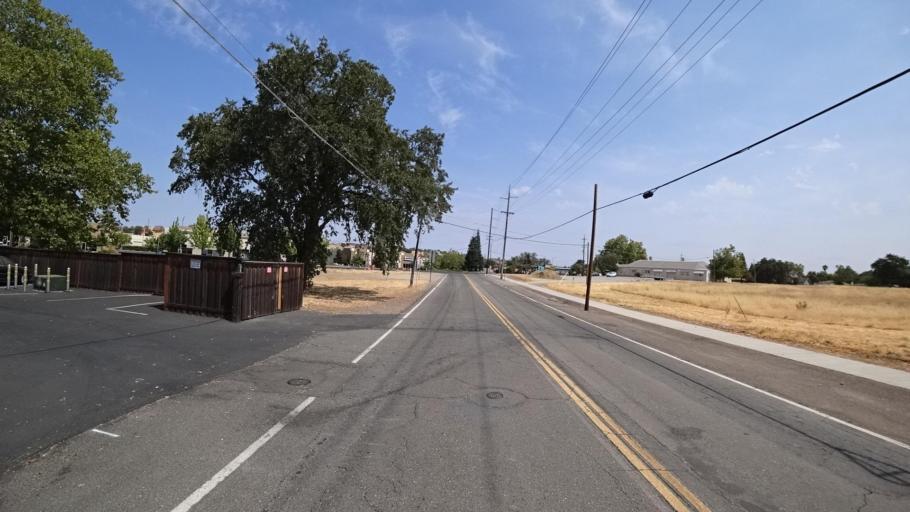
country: US
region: California
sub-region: Placer County
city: Rocklin
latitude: 38.7969
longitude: -121.2290
